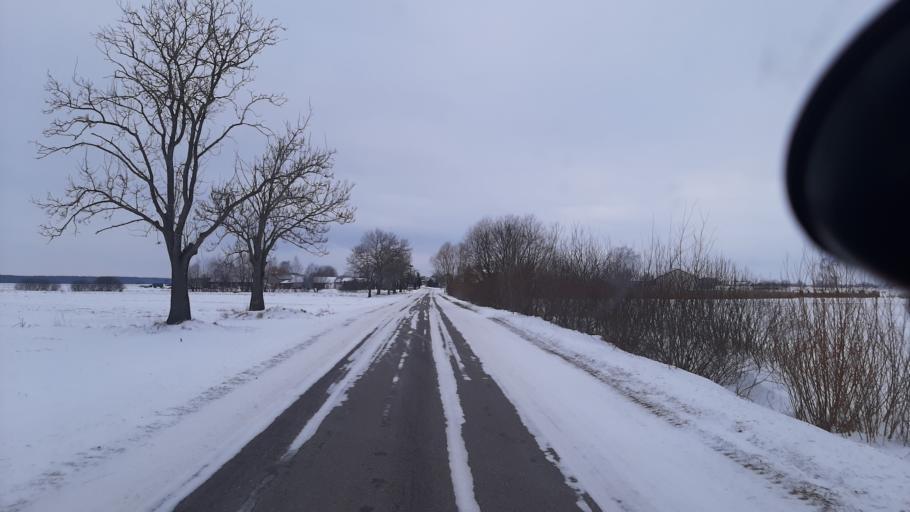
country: PL
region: Lublin Voivodeship
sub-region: Powiat lubartowski
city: Abramow
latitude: 51.4393
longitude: 22.3017
